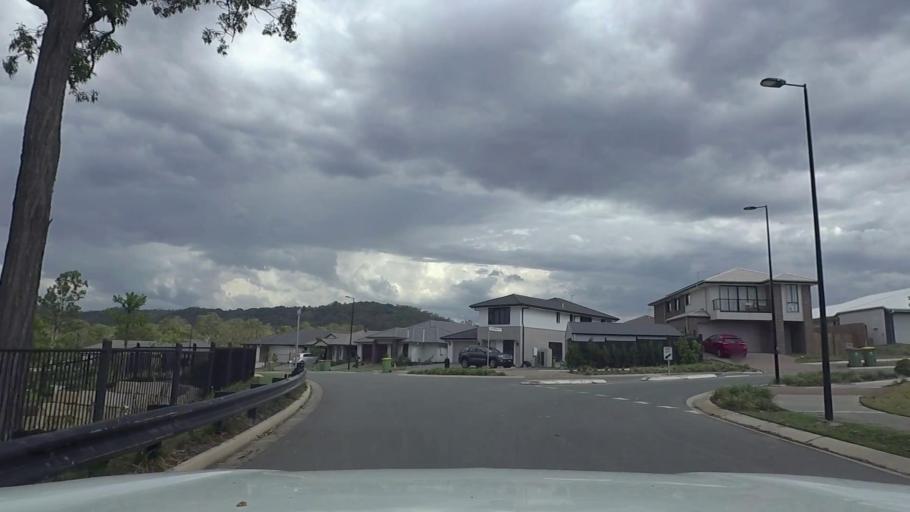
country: AU
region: Queensland
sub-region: Logan
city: Windaroo
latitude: -27.7309
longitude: 153.1661
